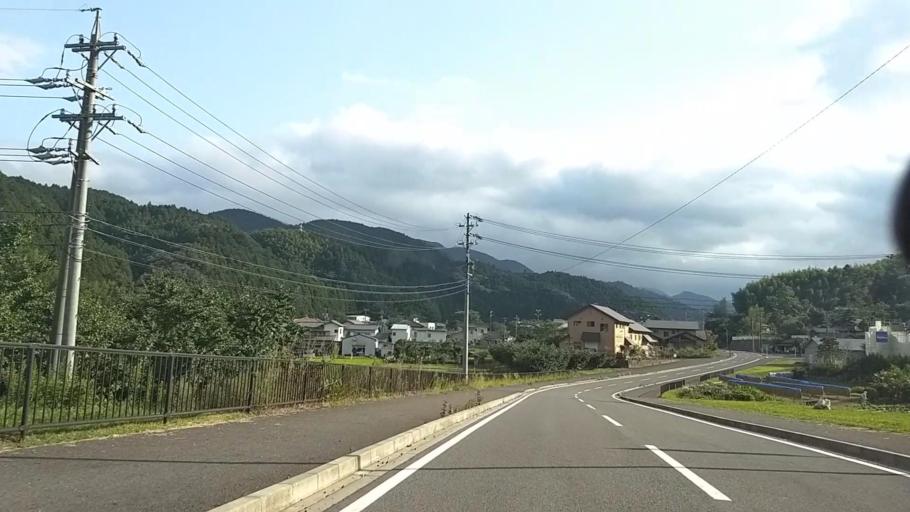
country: JP
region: Shizuoka
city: Fujinomiya
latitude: 35.1961
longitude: 138.5511
